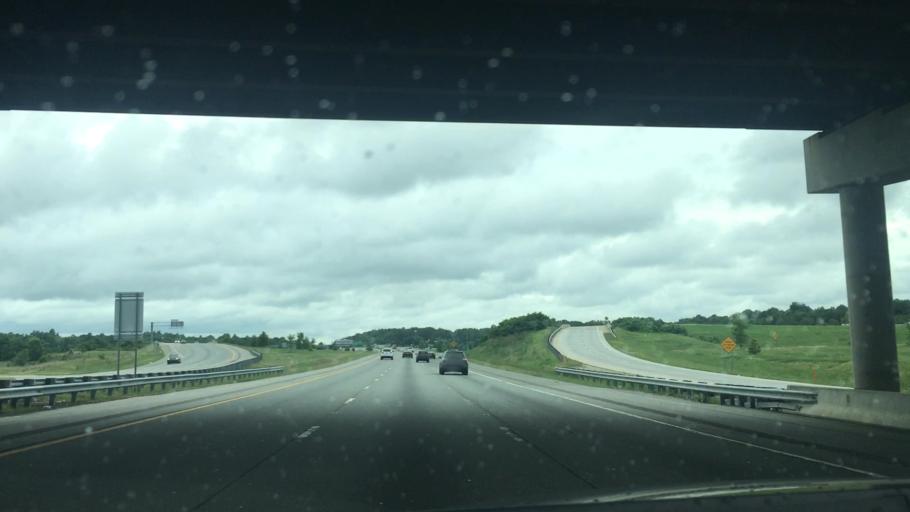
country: US
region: North Carolina
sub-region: Guilford County
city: Jamestown
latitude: 36.0054
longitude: -79.8516
